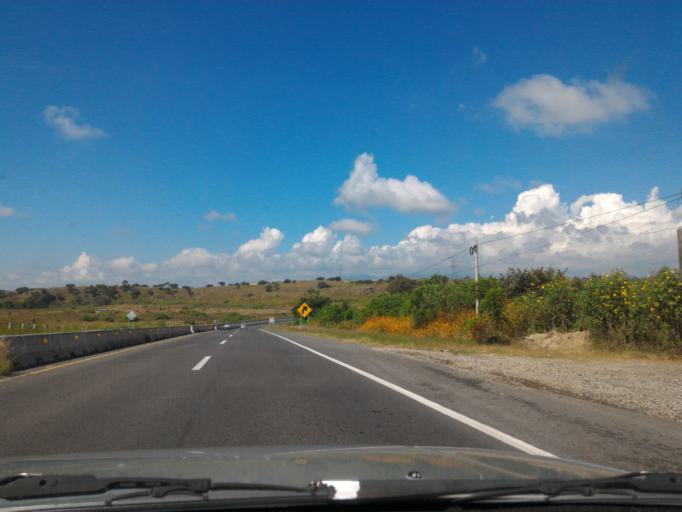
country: MX
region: Jalisco
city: La Venta del Astillero
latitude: 20.7319
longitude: -103.6171
